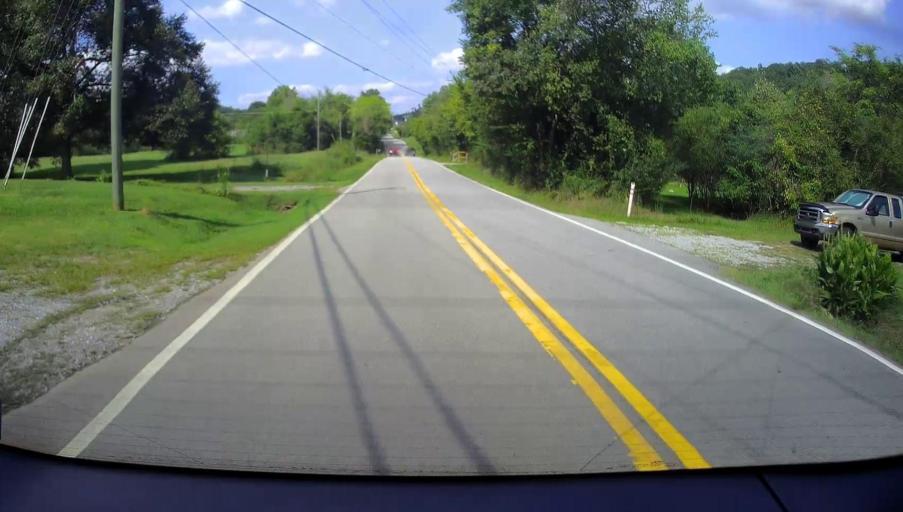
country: US
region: Georgia
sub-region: Catoosa County
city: Ringgold
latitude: 34.9326
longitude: -85.0853
